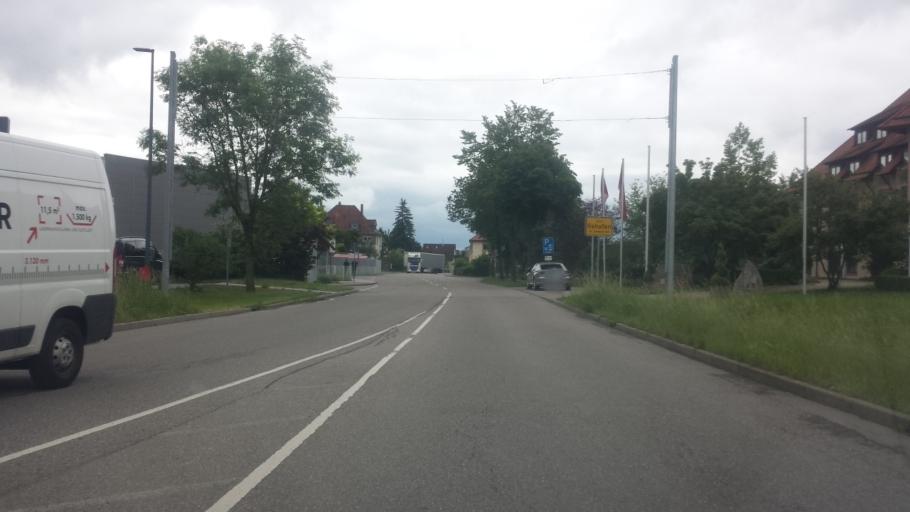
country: DE
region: Baden-Wuerttemberg
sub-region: Regierungsbezirk Stuttgart
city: Ilshofen
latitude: 49.1724
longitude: 9.9149
